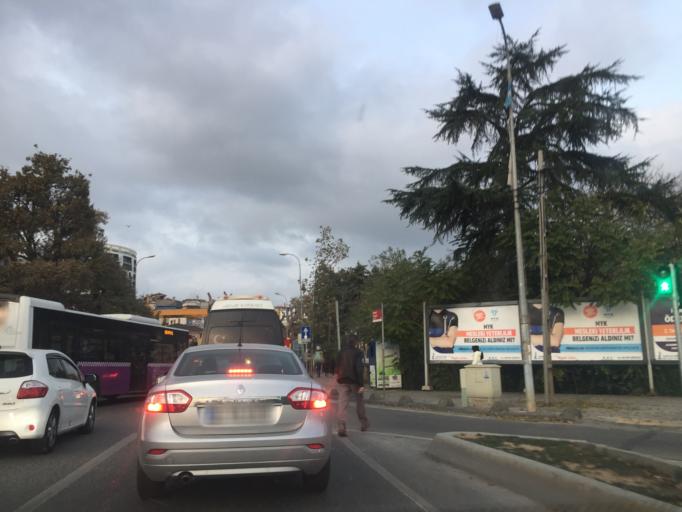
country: TR
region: Istanbul
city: Samandira
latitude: 40.9837
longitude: 29.2317
